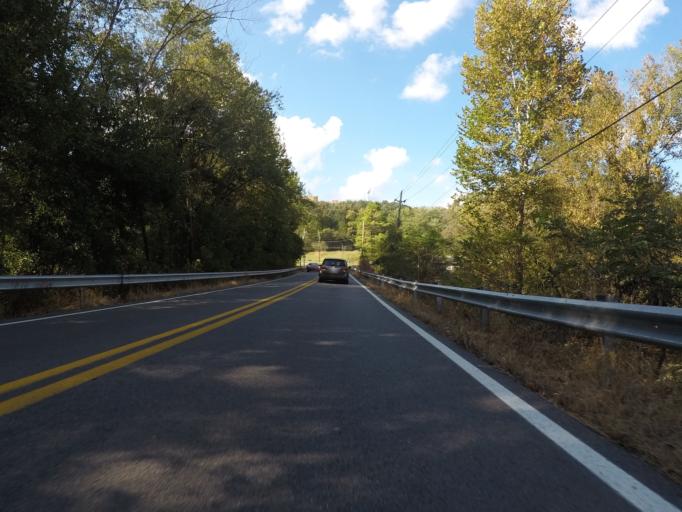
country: US
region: Ohio
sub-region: Lawrence County
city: Burlington
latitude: 38.3706
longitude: -82.5131
